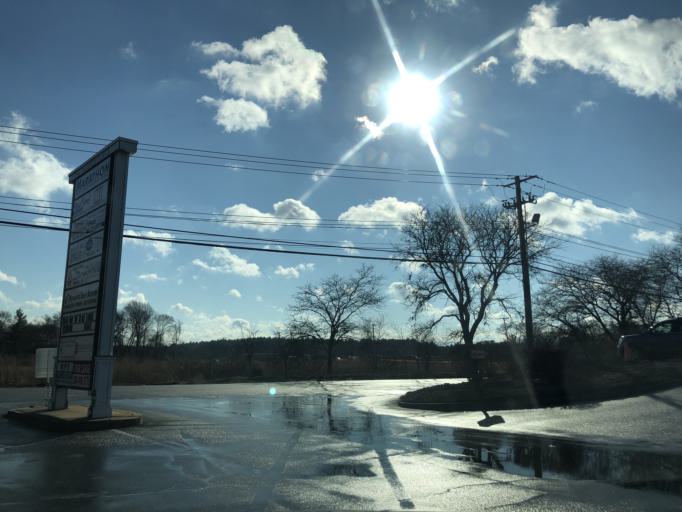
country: US
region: Massachusetts
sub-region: Bristol County
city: Norton Center
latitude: 41.9861
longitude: -71.1570
